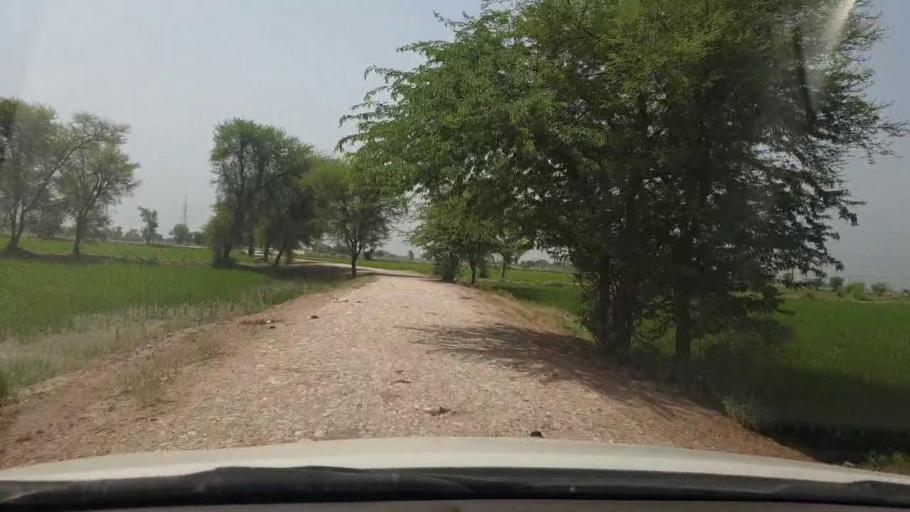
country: PK
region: Sindh
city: Shikarpur
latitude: 28.0160
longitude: 68.6501
